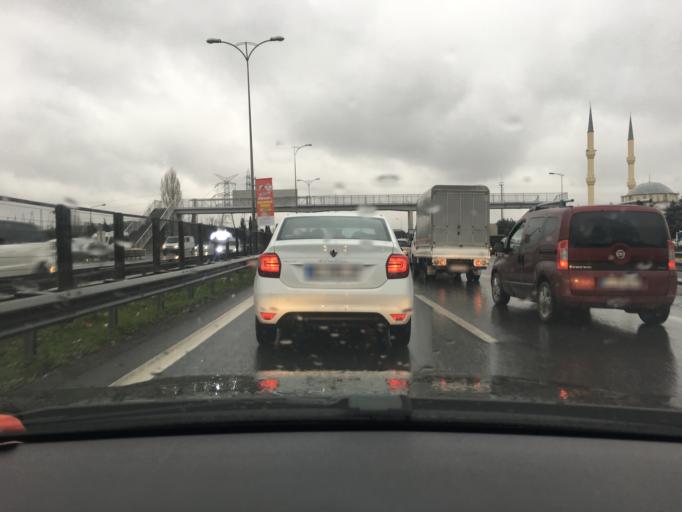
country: TR
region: Istanbul
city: Esenler
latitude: 41.0487
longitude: 28.8851
